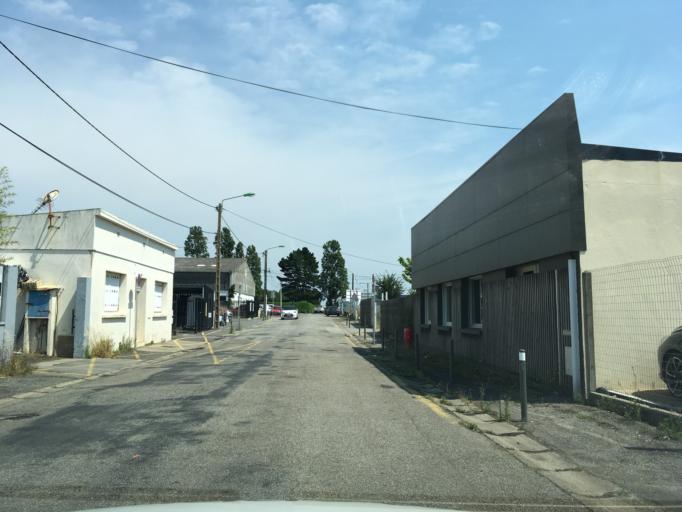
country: FR
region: Brittany
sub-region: Departement du Morbihan
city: Queven
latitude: 47.7637
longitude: -3.4040
